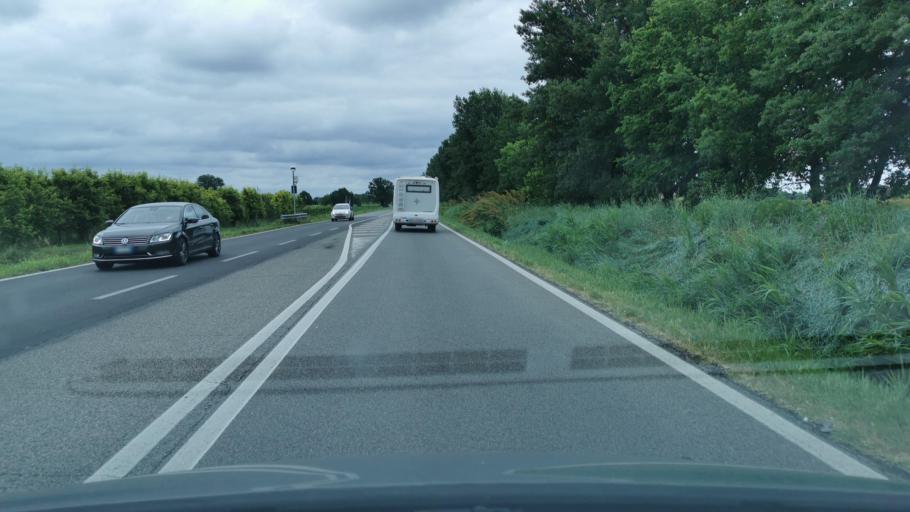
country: IT
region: Emilia-Romagna
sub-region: Provincia di Ravenna
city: Granarolo
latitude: 44.3441
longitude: 11.9225
